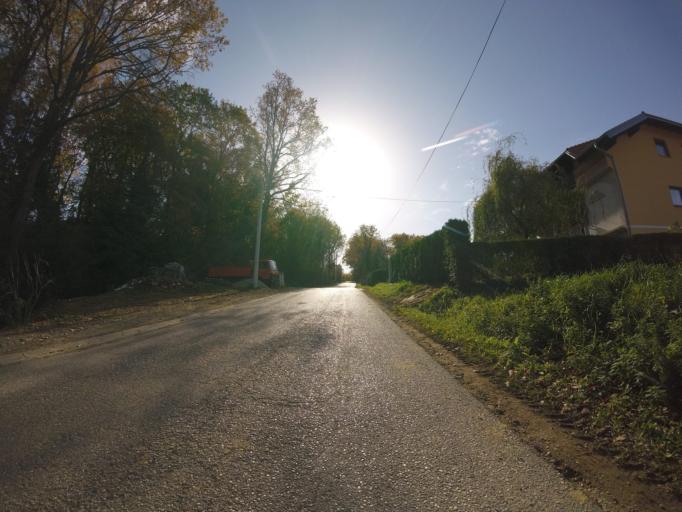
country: HR
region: Zagrebacka
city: Gradici
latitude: 45.6178
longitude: 16.0176
